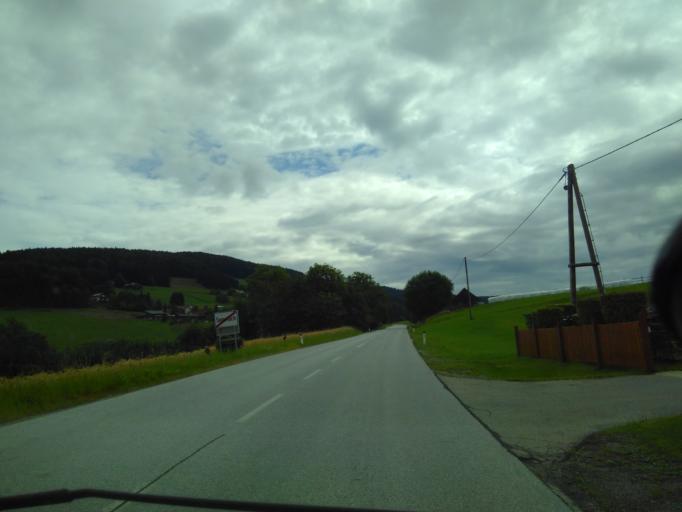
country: AT
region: Styria
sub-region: Politischer Bezirk Graz-Umgebung
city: Semriach
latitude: 47.2174
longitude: 15.4137
